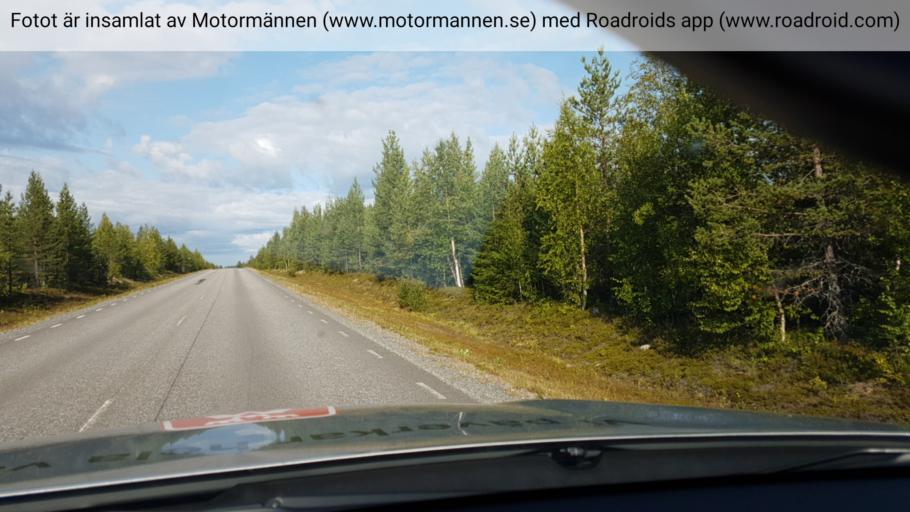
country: SE
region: Vaesterbotten
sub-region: Skelleftea Kommun
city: Storvik
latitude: 65.3261
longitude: 20.6871
